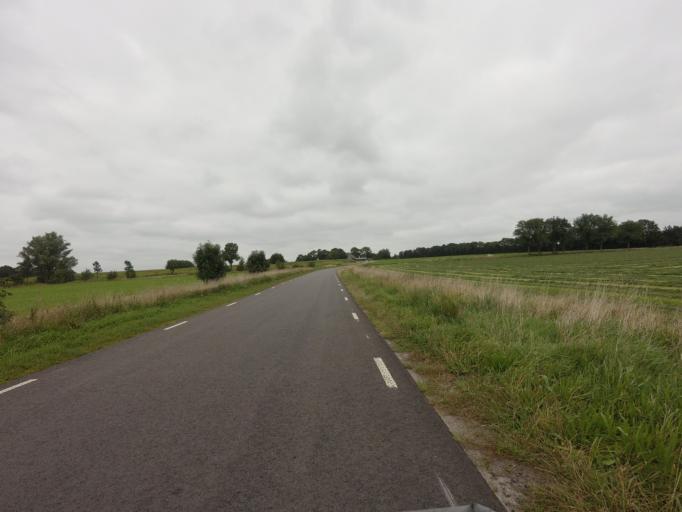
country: NL
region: Overijssel
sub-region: Gemeente Steenwijkerland
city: Steenwijkerwold
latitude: 52.7955
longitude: 6.0464
